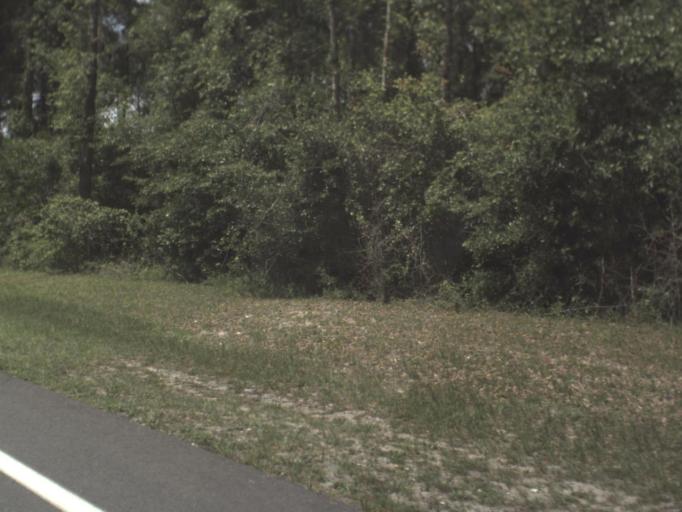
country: US
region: Florida
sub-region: Suwannee County
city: Wellborn
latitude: 30.3363
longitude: -82.7610
